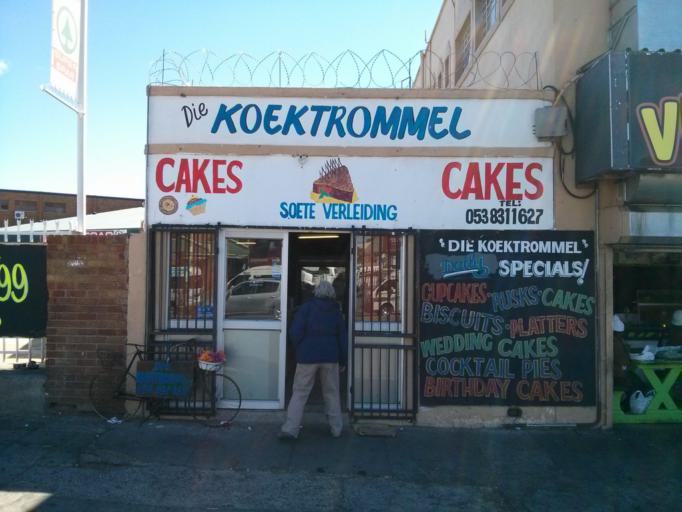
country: ZA
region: Northern Cape
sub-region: Frances Baard District Municipality
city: Kimberley
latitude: -28.7408
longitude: 24.7617
